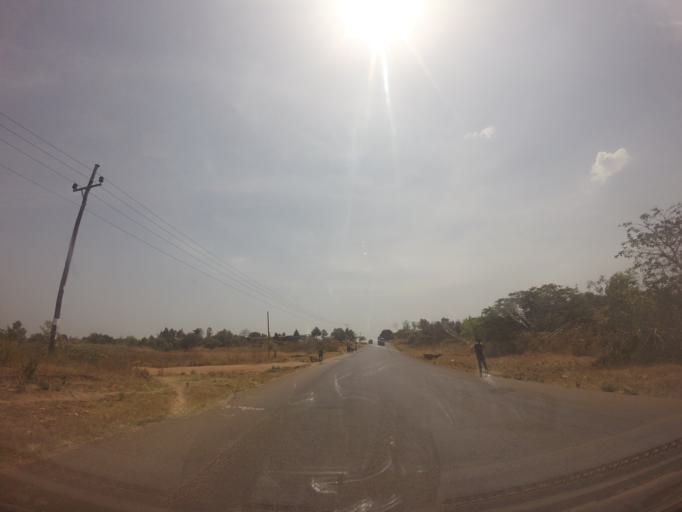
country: UG
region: Northern Region
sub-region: Arua District
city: Arua
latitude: 2.9569
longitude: 30.9255
